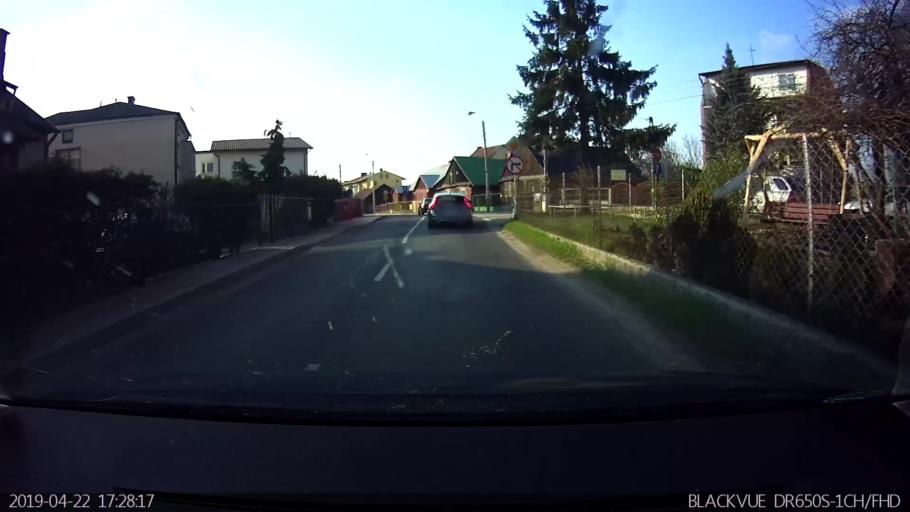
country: PL
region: Masovian Voivodeship
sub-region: Powiat sokolowski
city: Sokolow Podlaski
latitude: 52.4020
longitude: 22.2603
